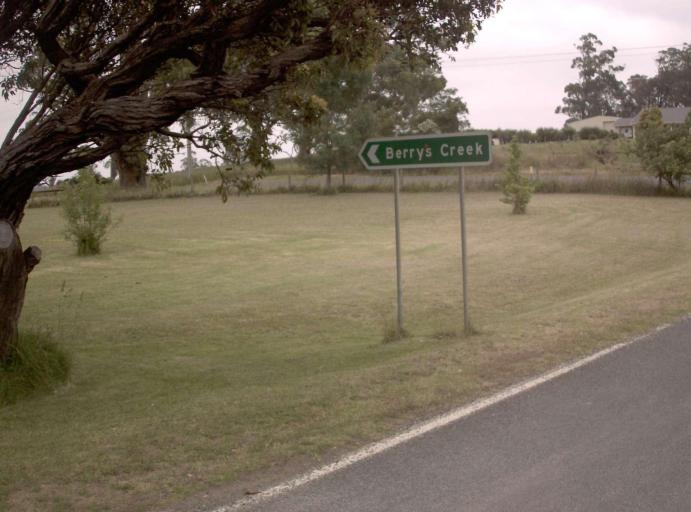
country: AU
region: Victoria
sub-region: Latrobe
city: Moe
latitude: -38.3978
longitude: 146.1483
